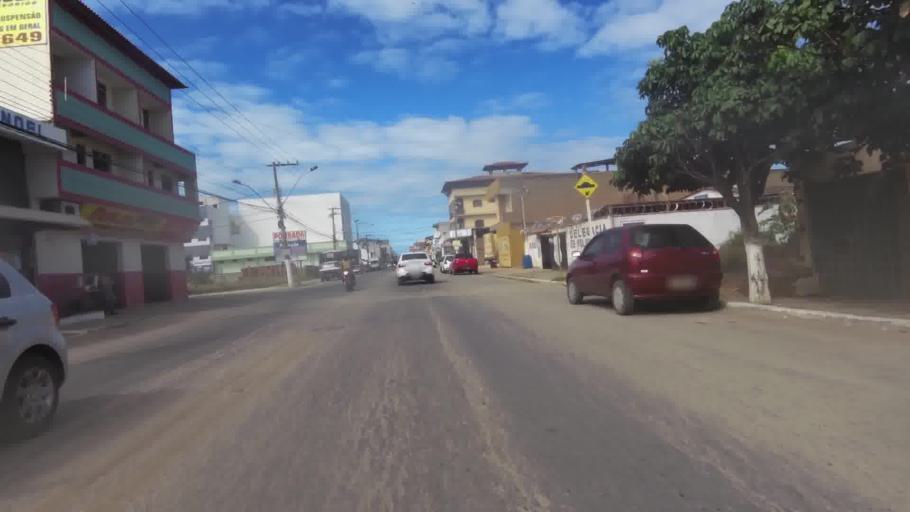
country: BR
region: Espirito Santo
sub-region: Marataizes
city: Marataizes
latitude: -21.0279
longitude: -40.8171
